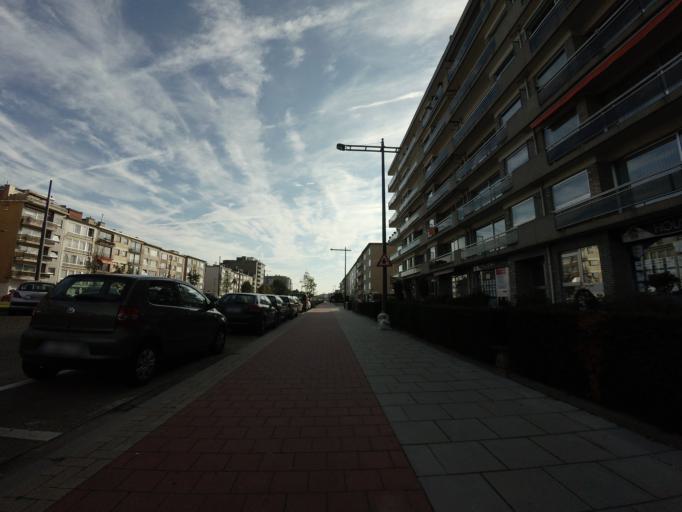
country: BE
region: Flanders
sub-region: Provincie Antwerpen
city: Schoten
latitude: 51.2311
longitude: 4.4788
